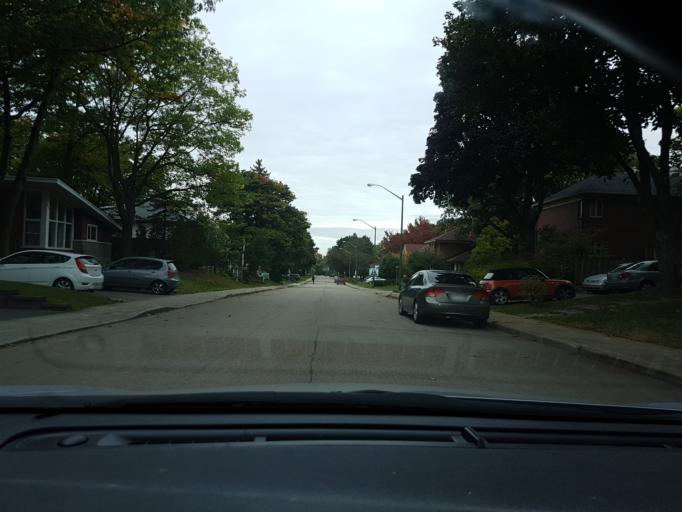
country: CA
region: Quebec
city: Quebec
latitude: 46.7869
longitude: -71.2630
